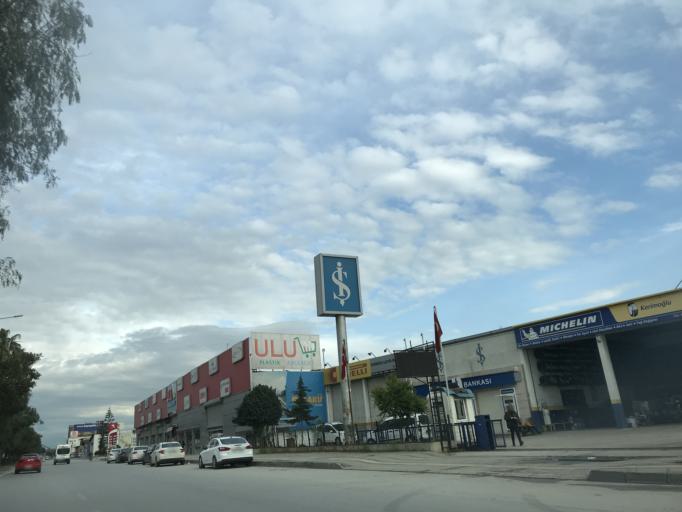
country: TR
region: Adana
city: Seyhan
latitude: 36.9947
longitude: 35.2805
